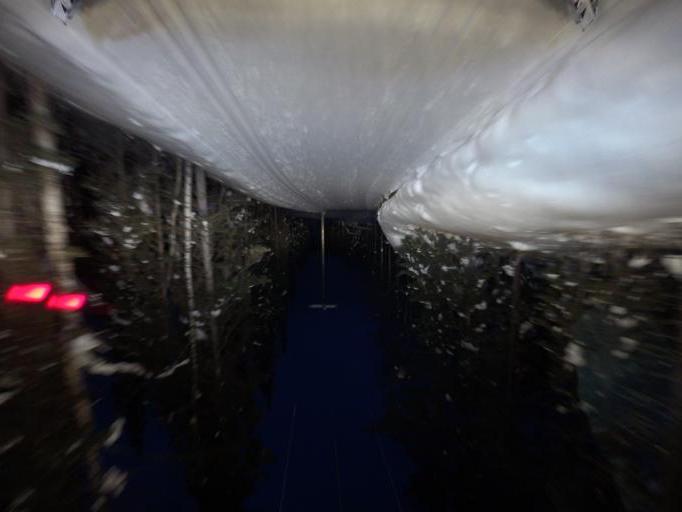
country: FI
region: Lapland
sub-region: Tunturi-Lappi
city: Kolari
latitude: 67.5853
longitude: 24.0854
